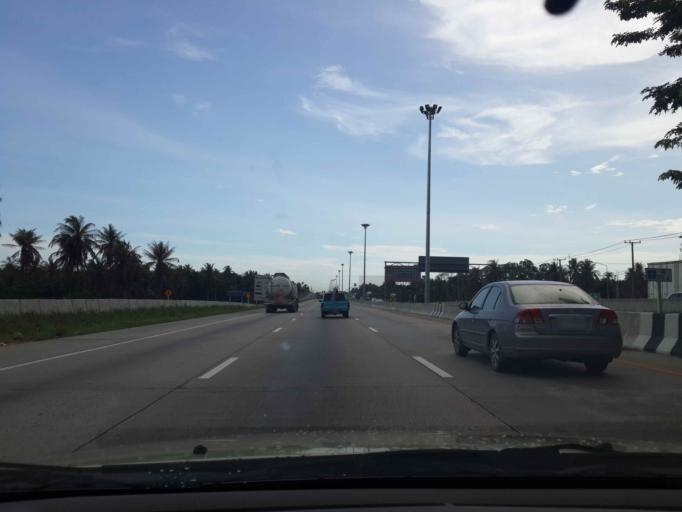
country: TH
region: Chon Buri
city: Bang Lamung
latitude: 12.9804
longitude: 100.9854
